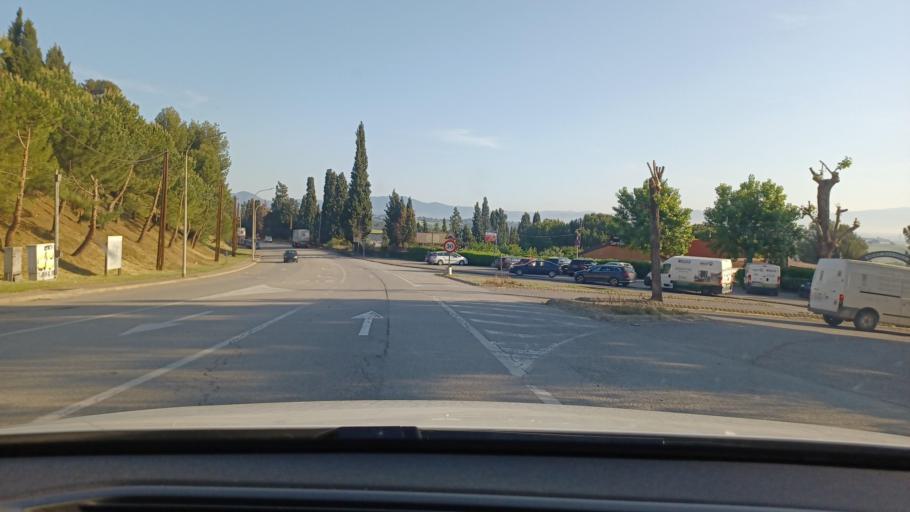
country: ES
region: Catalonia
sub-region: Provincia de Barcelona
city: Polinya
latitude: 41.5275
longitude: 2.1482
